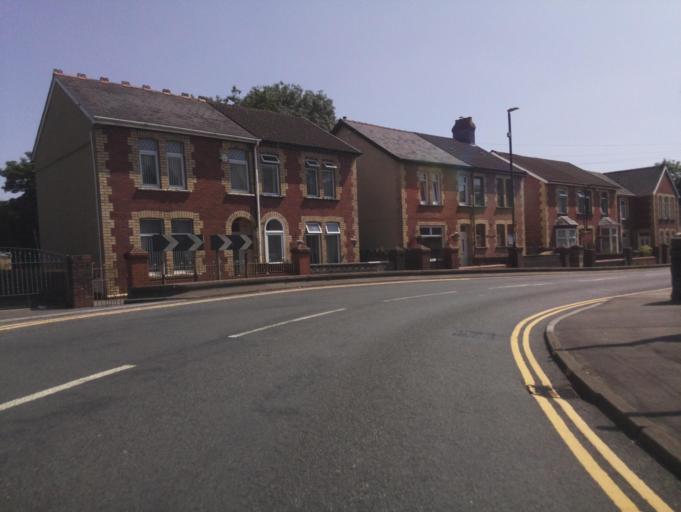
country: GB
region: Wales
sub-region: Caerphilly County Borough
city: Ystrad Mynach
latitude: 51.6392
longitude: -3.2348
